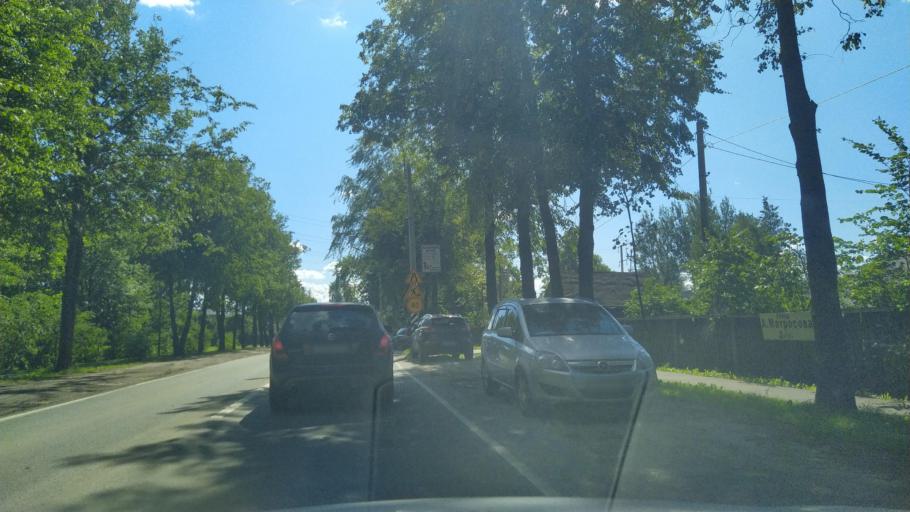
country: RU
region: St.-Petersburg
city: Pavlovsk
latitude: 59.6763
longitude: 30.4247
